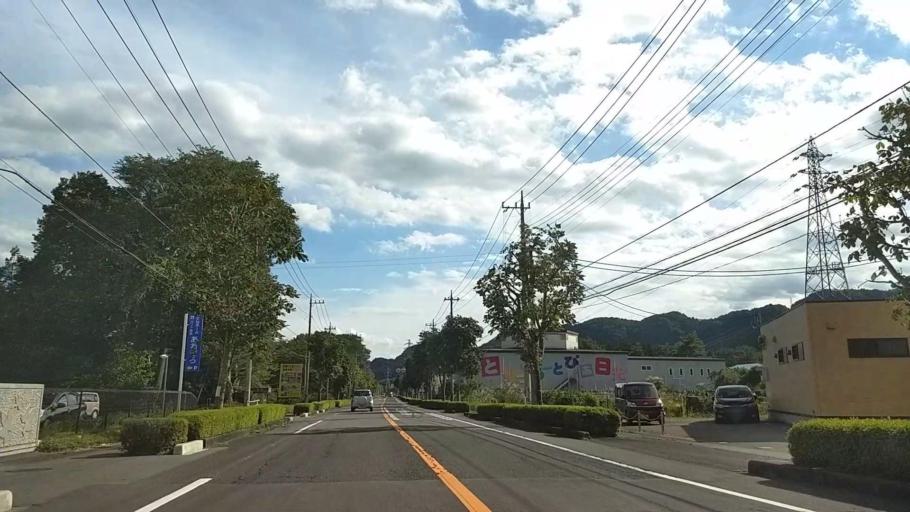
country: JP
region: Tochigi
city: Imaichi
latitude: 36.7901
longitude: 139.7020
